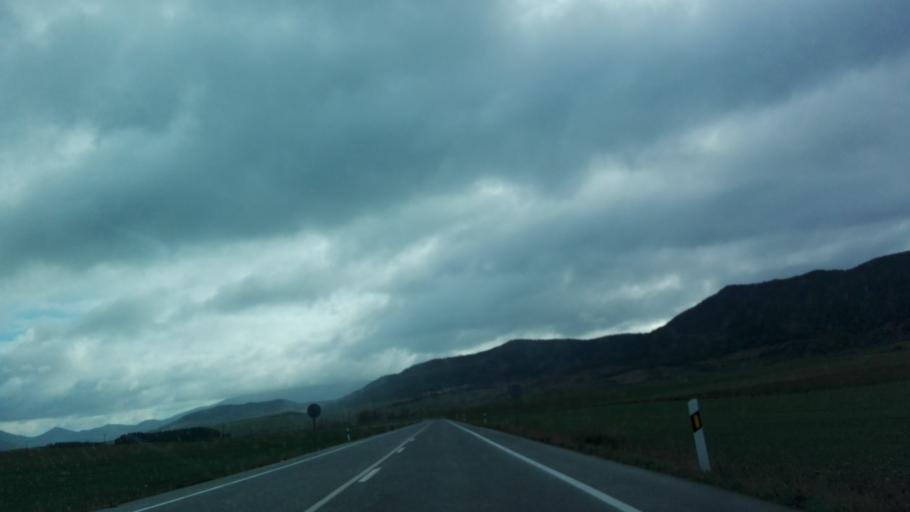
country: ES
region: Navarre
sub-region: Provincia de Navarra
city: Lizoain
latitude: 42.8104
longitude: -1.5037
